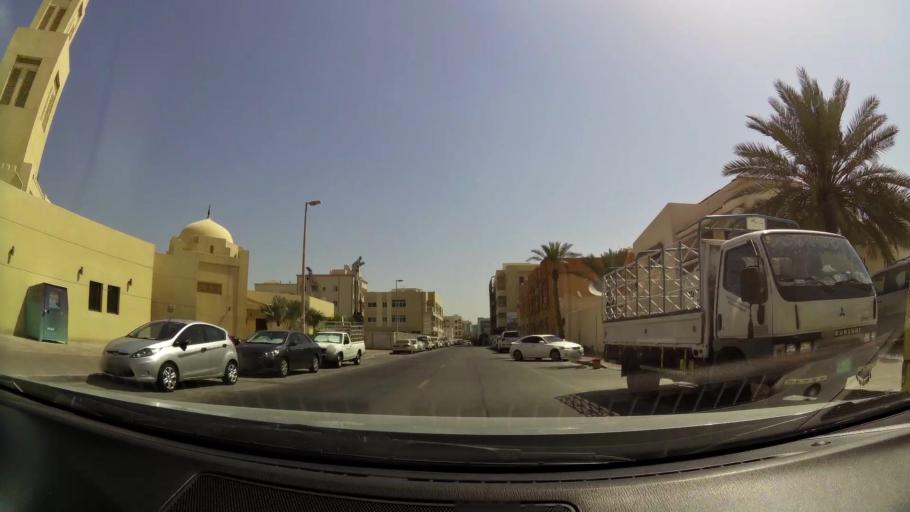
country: AE
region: Ash Shariqah
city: Sharjah
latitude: 25.2330
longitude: 55.2742
